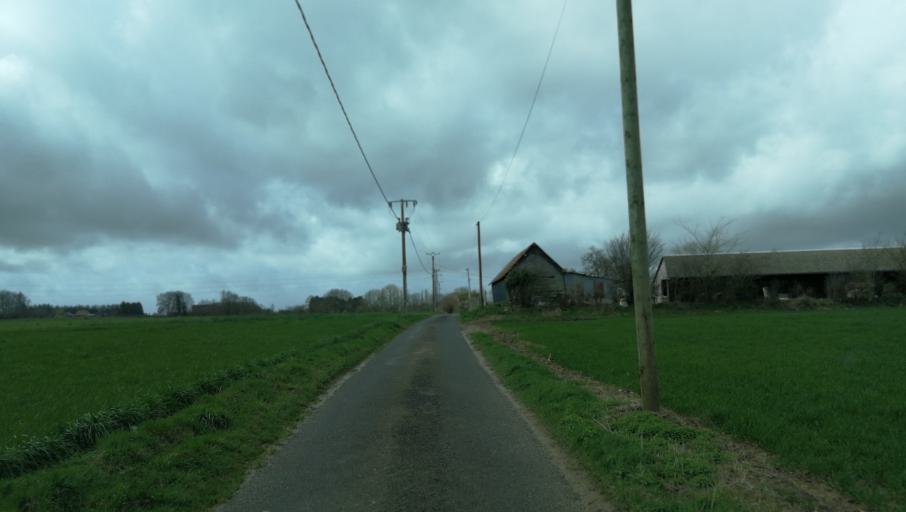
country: FR
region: Haute-Normandie
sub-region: Departement de l'Eure
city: Lieurey
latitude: 49.2331
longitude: 0.5320
